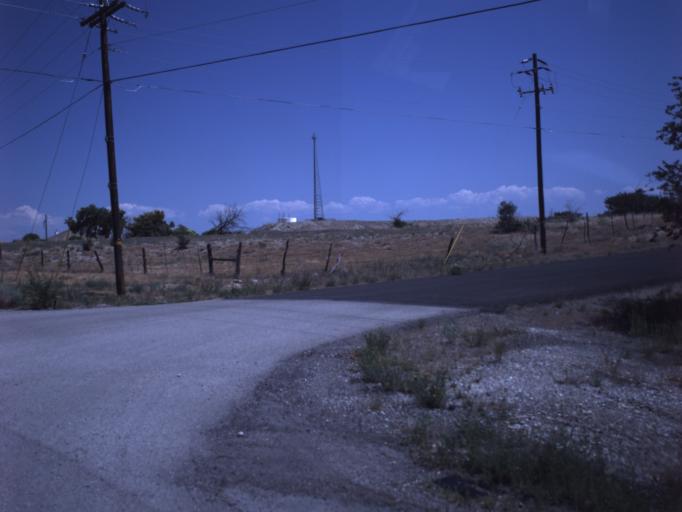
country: US
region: Utah
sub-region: Emery County
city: Ferron
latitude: 39.0989
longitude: -111.1320
